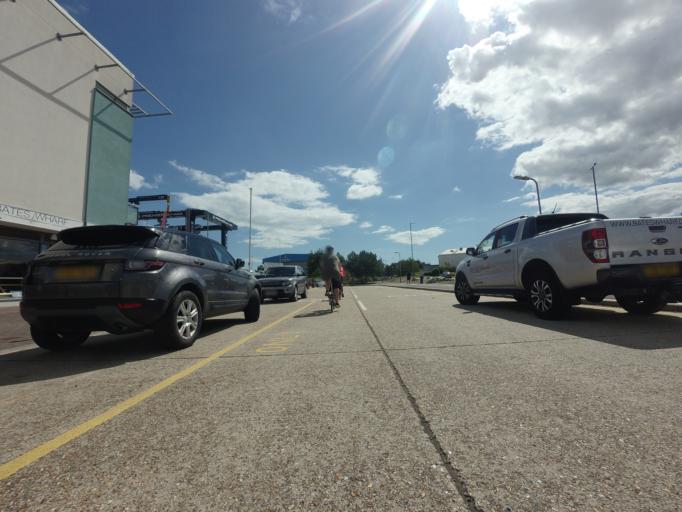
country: GB
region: England
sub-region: East Sussex
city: Pevensey
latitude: 50.7955
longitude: 0.3262
